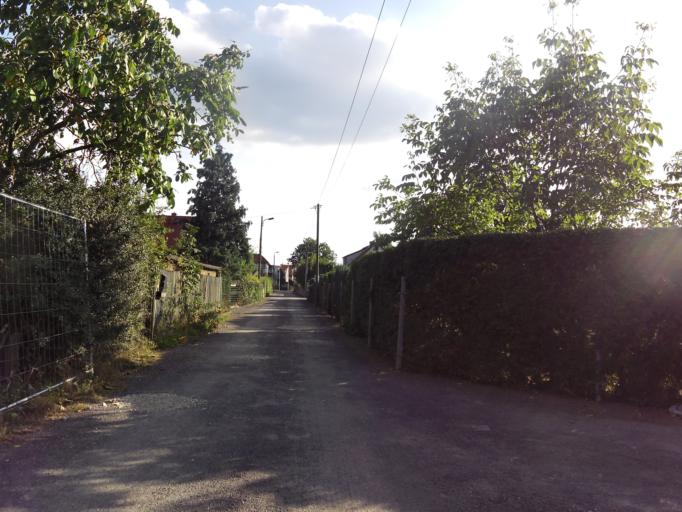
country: DE
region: Saxony
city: Markranstadt
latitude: 51.3463
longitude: 12.2738
